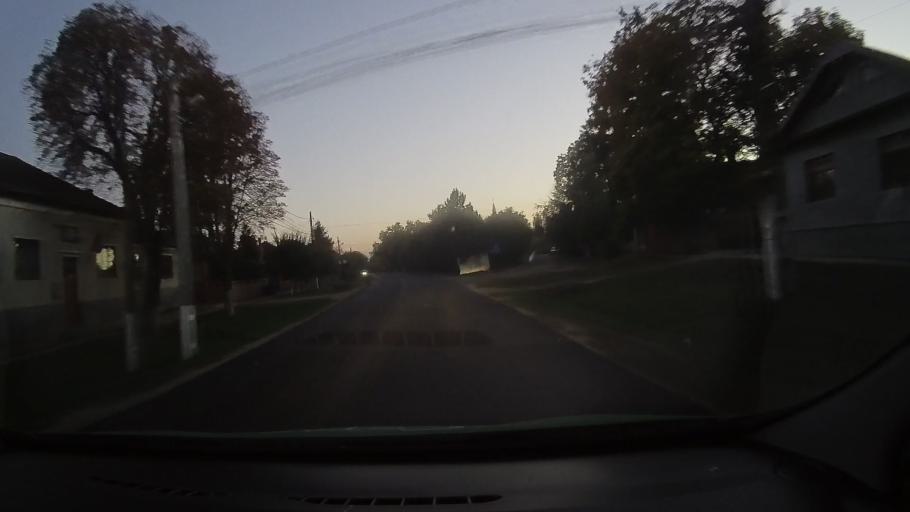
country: RO
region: Bihor
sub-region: Comuna Simian
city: Simian
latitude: 47.4961
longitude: 22.0897
